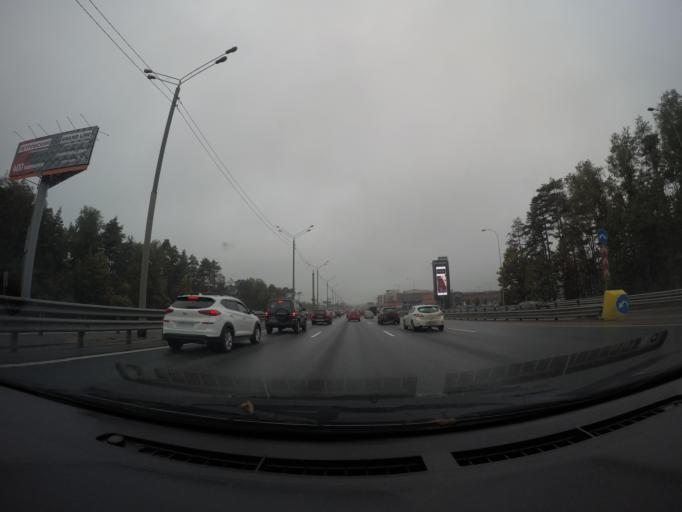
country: RU
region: Moskovskaya
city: Arkhangel'skoye
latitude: 55.8011
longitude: 37.2857
